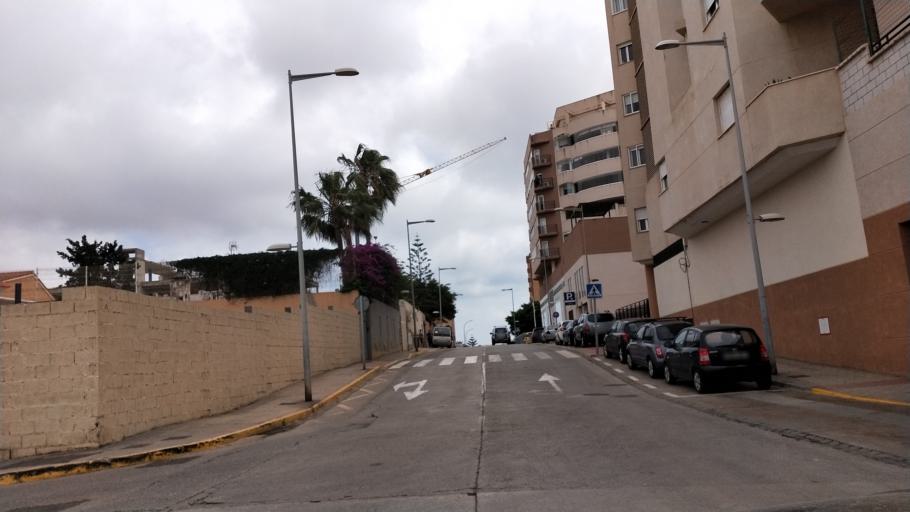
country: ES
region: Melilla
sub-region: Melilla
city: Melilla
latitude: 35.2876
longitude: -2.9553
